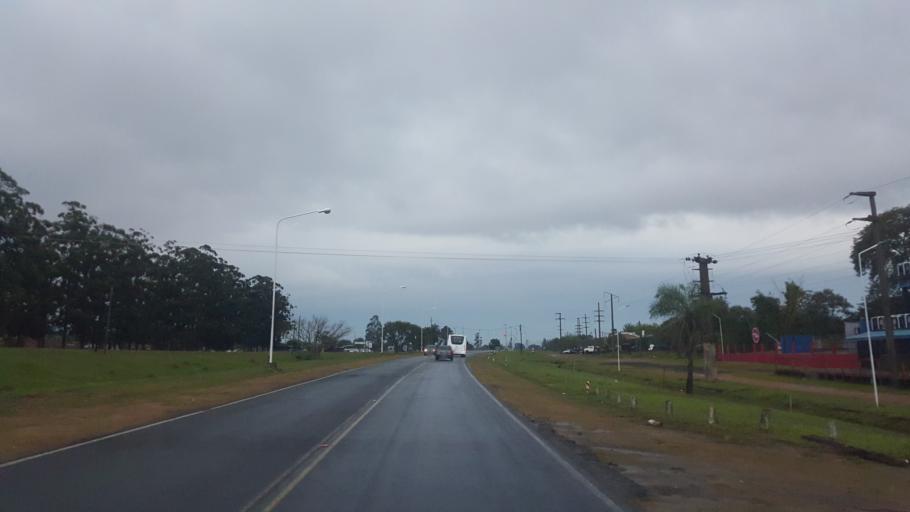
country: AR
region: Corrientes
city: Ituzaingo
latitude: -27.5740
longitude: -56.6714
